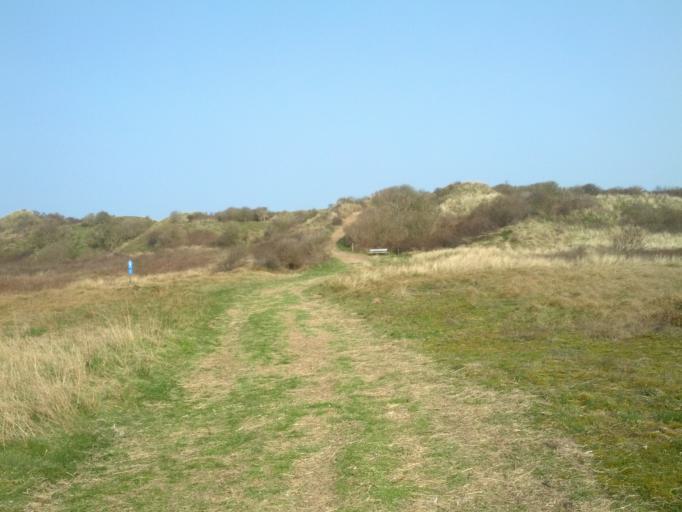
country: DE
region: Lower Saxony
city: Spiekeroog
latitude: 53.7532
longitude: 7.5907
